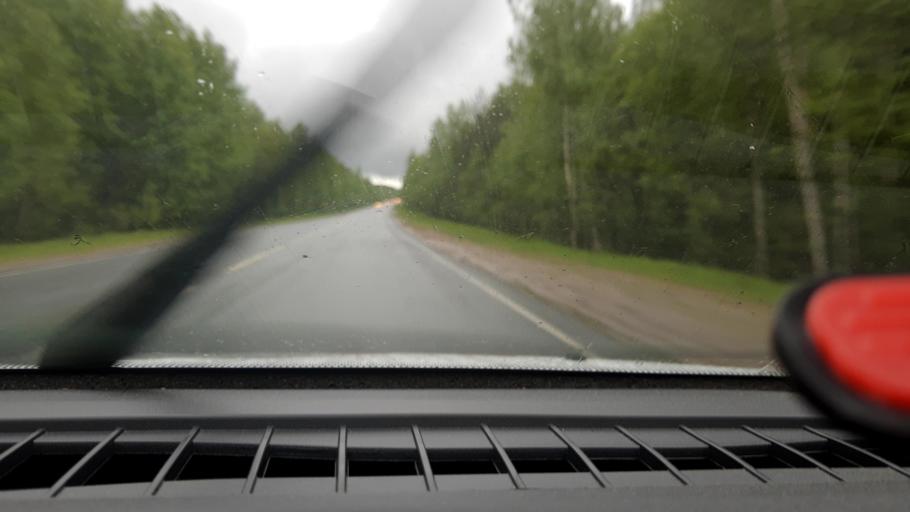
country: RU
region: Nizjnij Novgorod
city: Semenov
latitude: 56.7786
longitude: 44.4300
